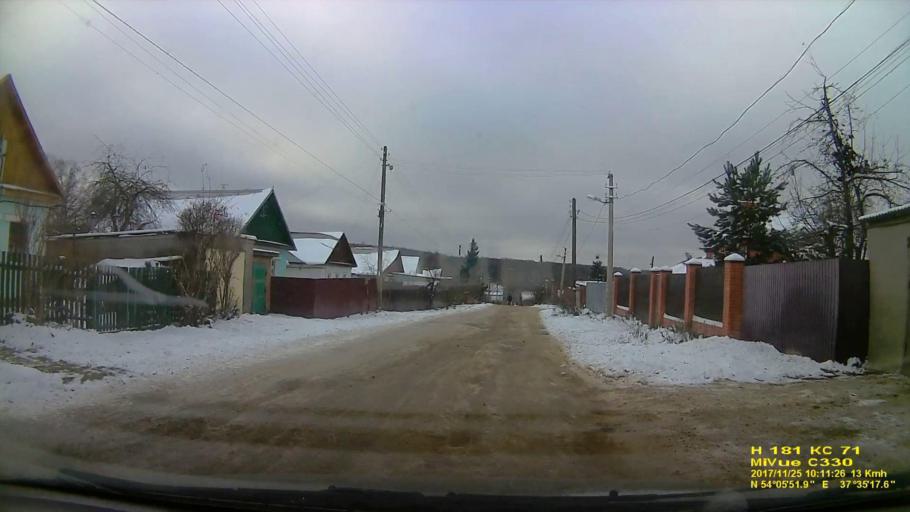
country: RU
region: Tula
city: Skuratovskiy
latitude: 54.0976
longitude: 37.5881
